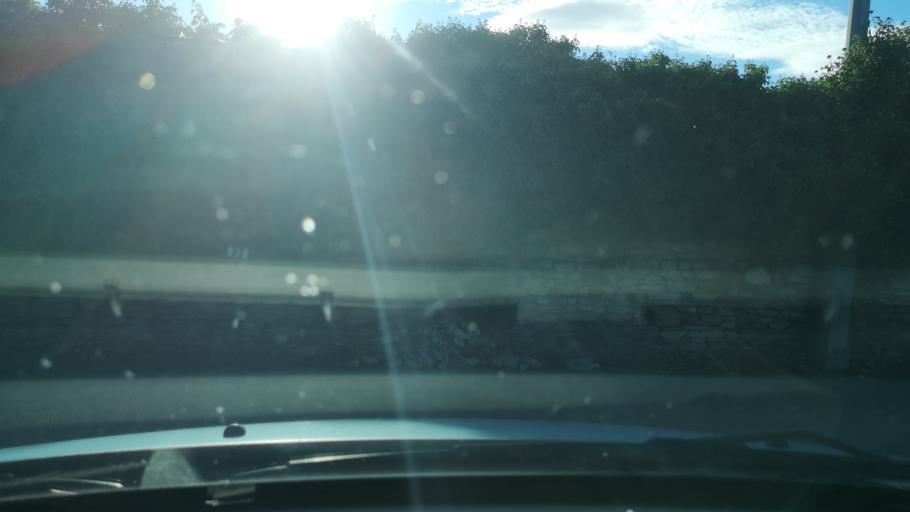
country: GB
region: England
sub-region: Doncaster
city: Campsall
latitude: 53.6225
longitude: -1.1792
